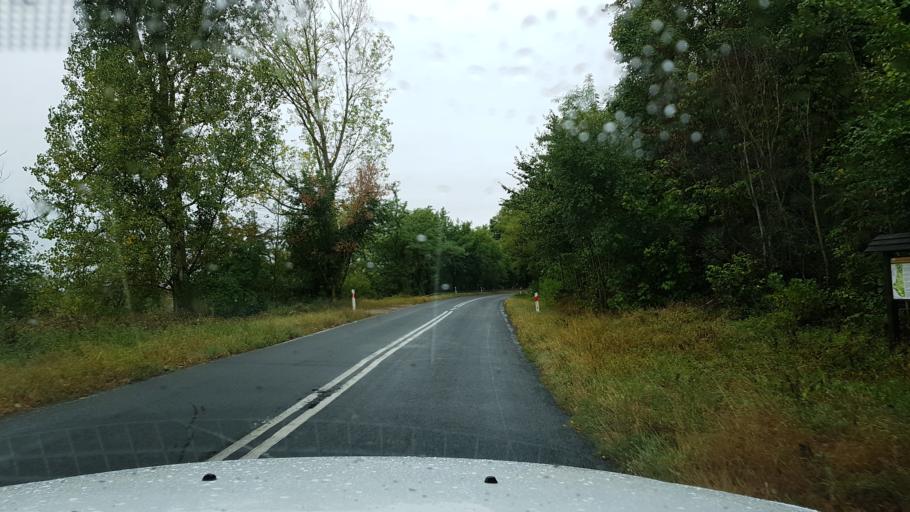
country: PL
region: West Pomeranian Voivodeship
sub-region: Powiat gryfinski
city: Cedynia
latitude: 52.8335
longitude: 14.1293
